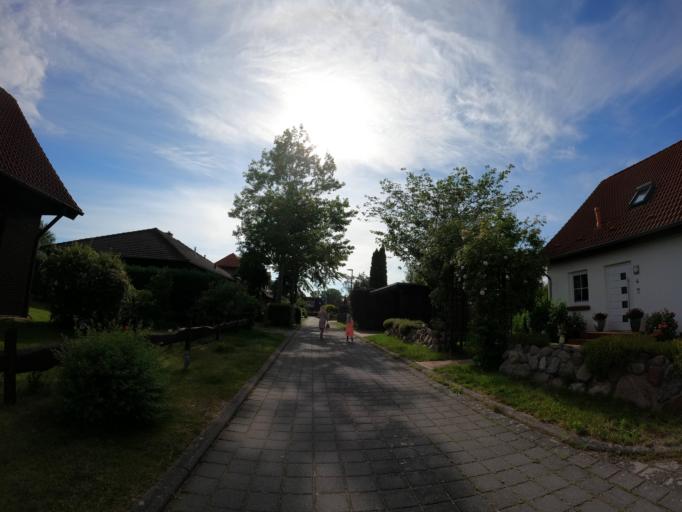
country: DE
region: Mecklenburg-Vorpommern
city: Prohn
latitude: 54.3504
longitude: 13.0147
